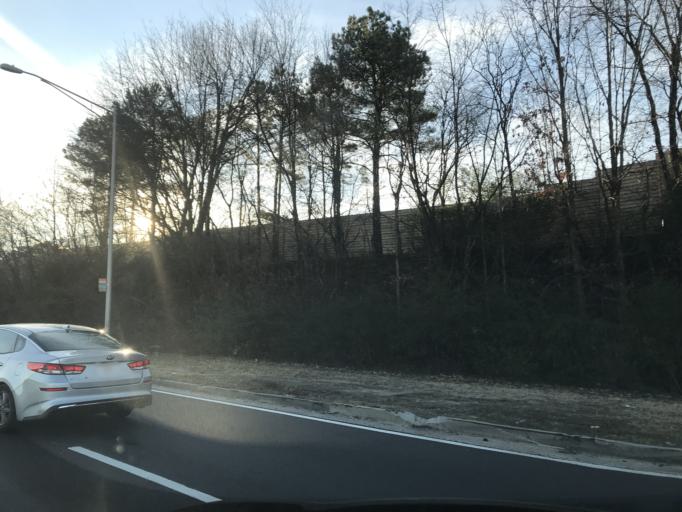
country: US
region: Georgia
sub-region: Fulton County
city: College Park
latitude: 33.6178
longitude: -84.4495
